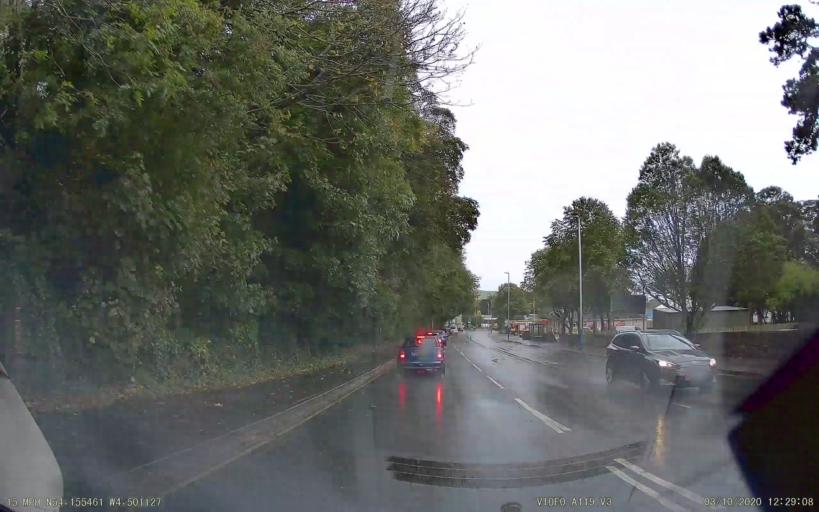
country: IM
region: Douglas
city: Douglas
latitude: 54.1556
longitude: -4.5011
